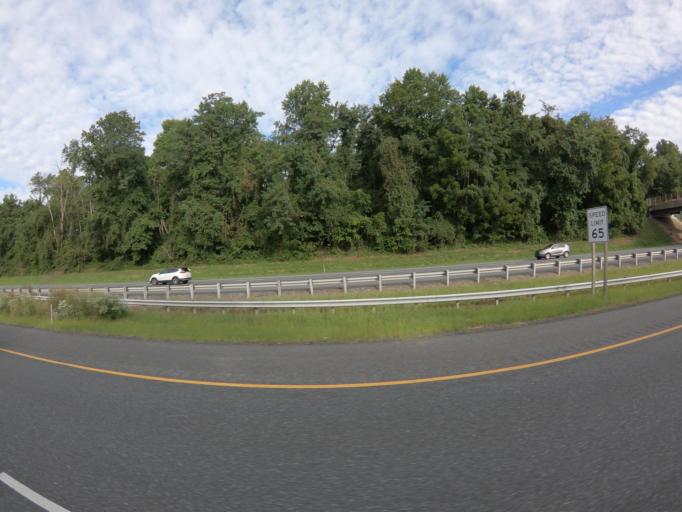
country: US
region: Maryland
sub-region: Harford County
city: Aberdeen
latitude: 39.5408
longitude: -76.1799
